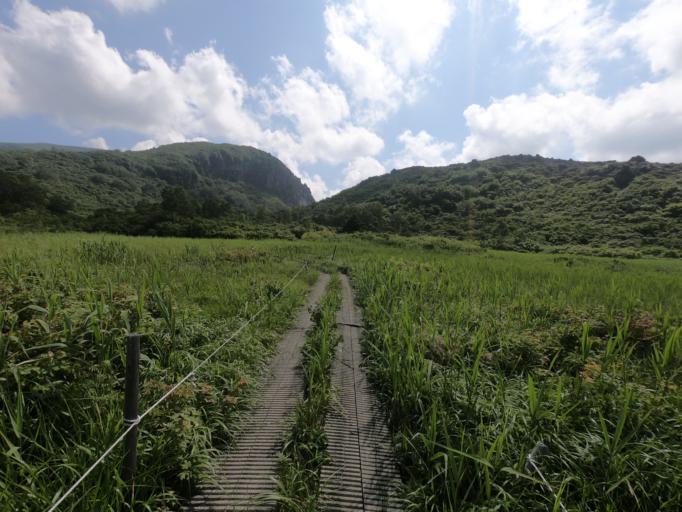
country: JP
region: Akita
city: Yuzawa
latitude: 38.9757
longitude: 140.7774
